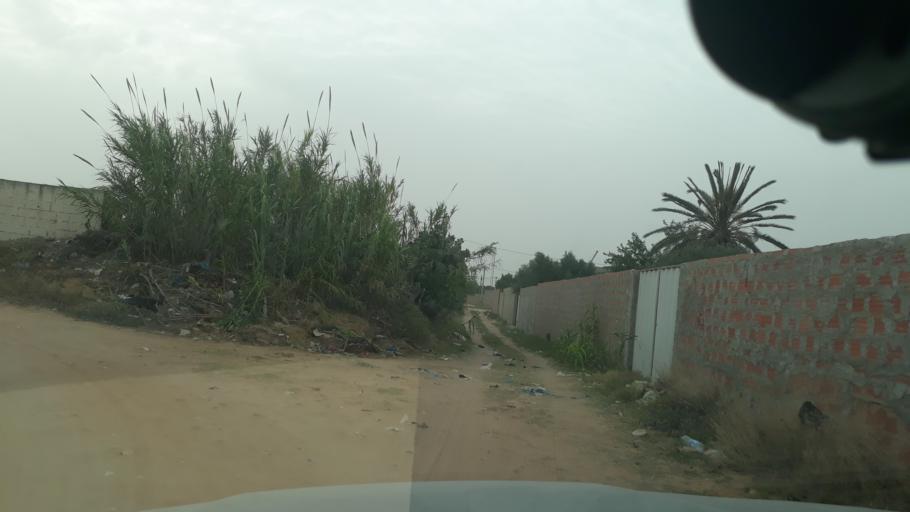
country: TN
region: Safaqis
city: Al Qarmadah
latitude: 34.7831
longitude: 10.7693
